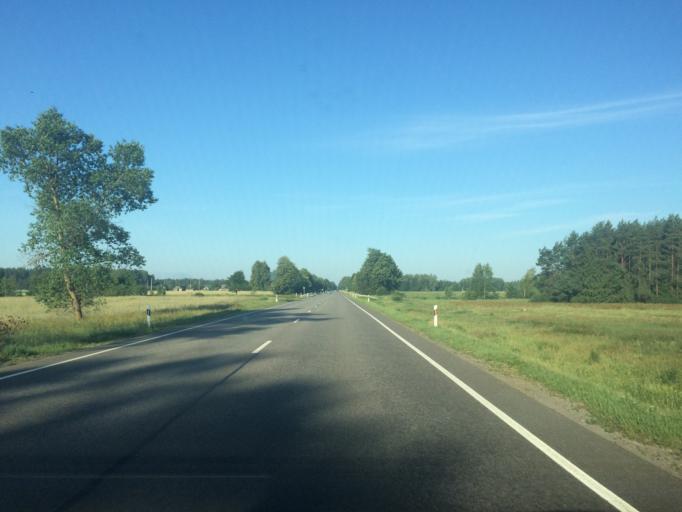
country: LT
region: Kauno apskritis
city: Jonava
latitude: 55.1392
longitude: 24.4379
